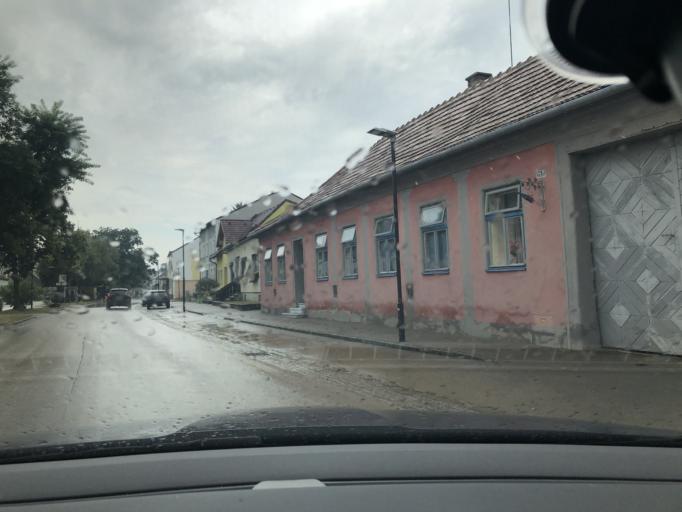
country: AT
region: Lower Austria
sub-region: Politischer Bezirk Ganserndorf
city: Auersthal
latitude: 48.3722
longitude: 16.6418
